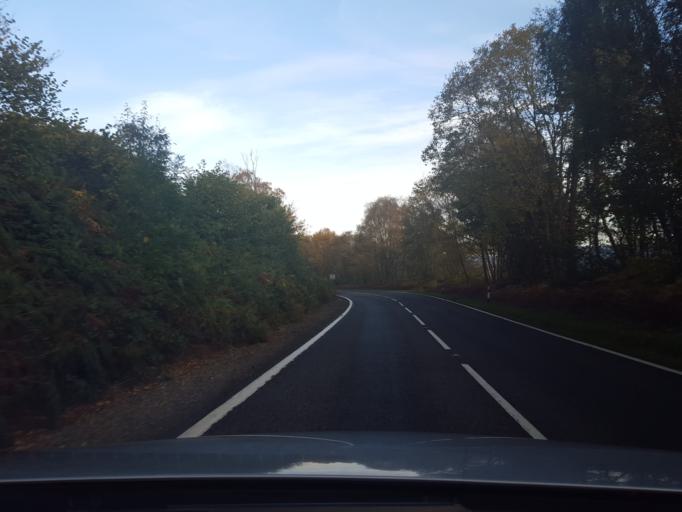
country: GB
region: Scotland
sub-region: Highland
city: Beauly
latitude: 57.3602
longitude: -4.3972
